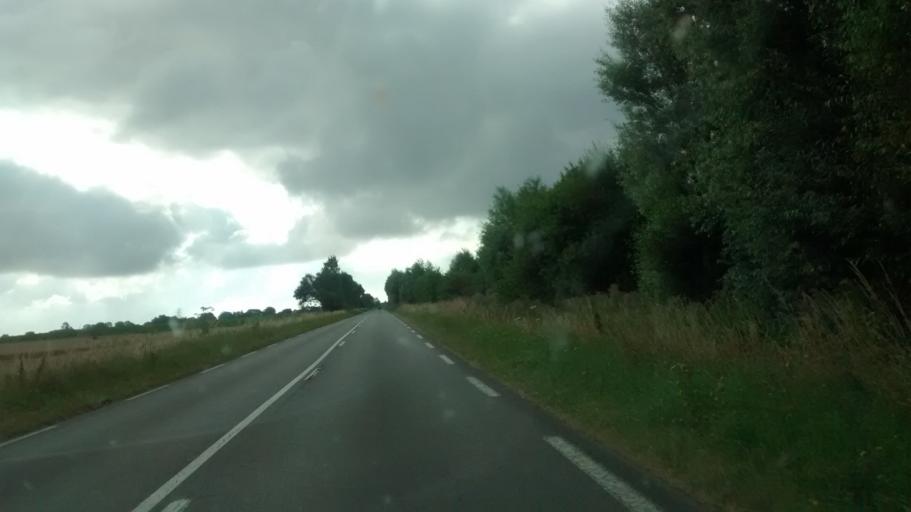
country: FR
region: Brittany
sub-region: Departement d'Ille-et-Vilaine
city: La Gouesniere
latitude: 48.5993
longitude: -1.8842
